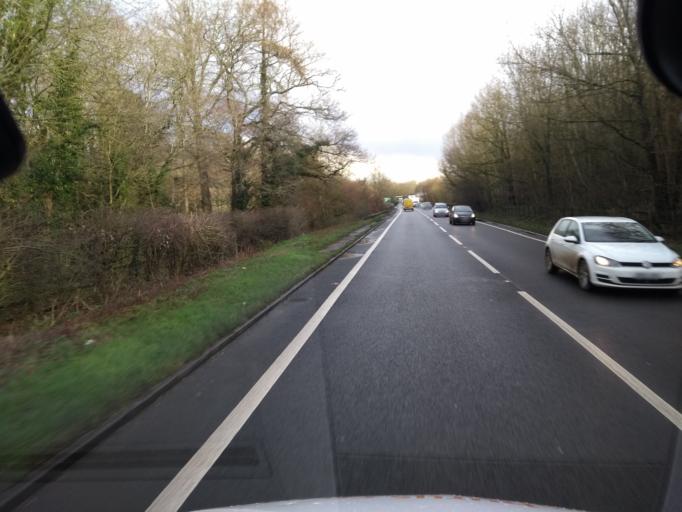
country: GB
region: England
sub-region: Somerset
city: Creech Saint Michael
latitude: 50.9814
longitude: -3.0075
